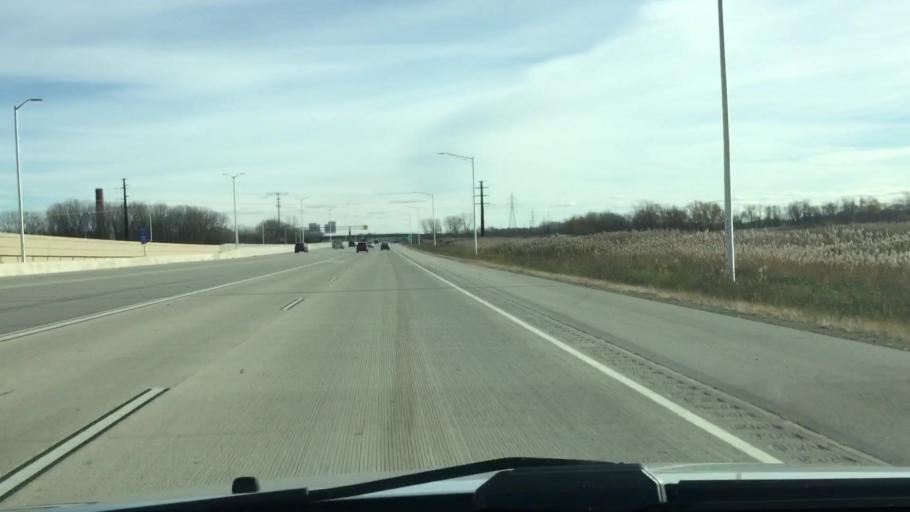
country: US
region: Wisconsin
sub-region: Brown County
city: Howard
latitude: 44.5566
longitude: -88.0486
